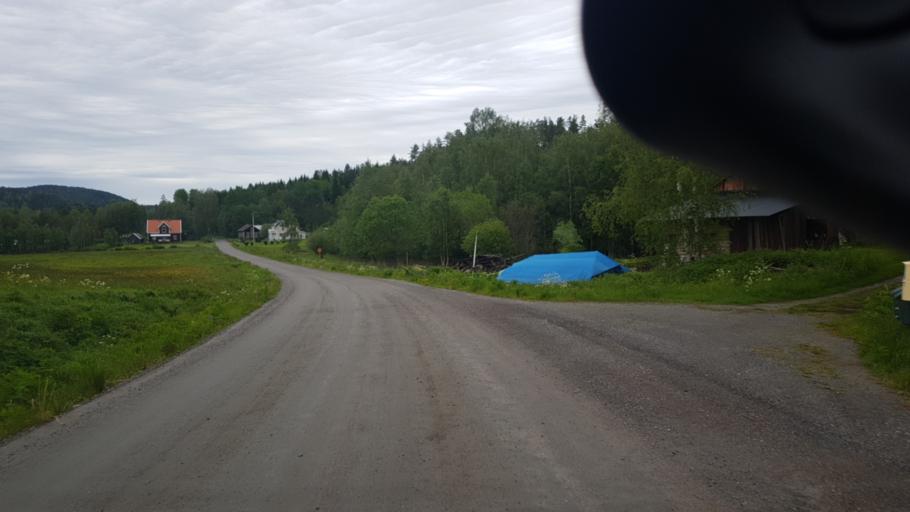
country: NO
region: Ostfold
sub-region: Romskog
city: Romskog
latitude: 59.6692
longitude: 11.9327
